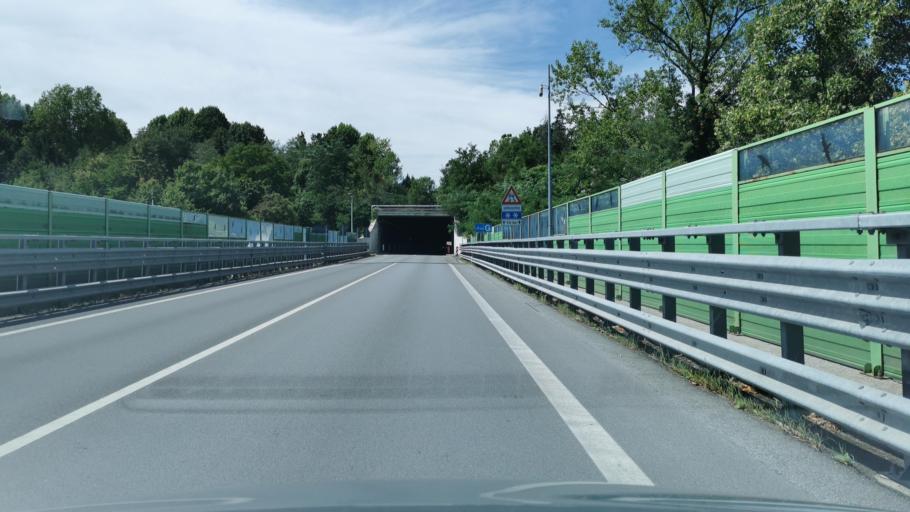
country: IT
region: Piedmont
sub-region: Provincia di Cuneo
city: Cuneo
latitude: 44.3725
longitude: 7.5435
